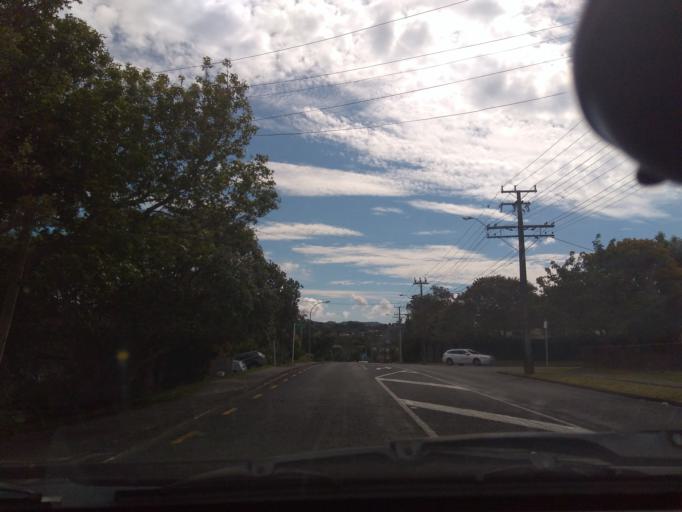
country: NZ
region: Auckland
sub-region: Auckland
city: Waitakere
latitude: -36.9266
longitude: 174.6750
